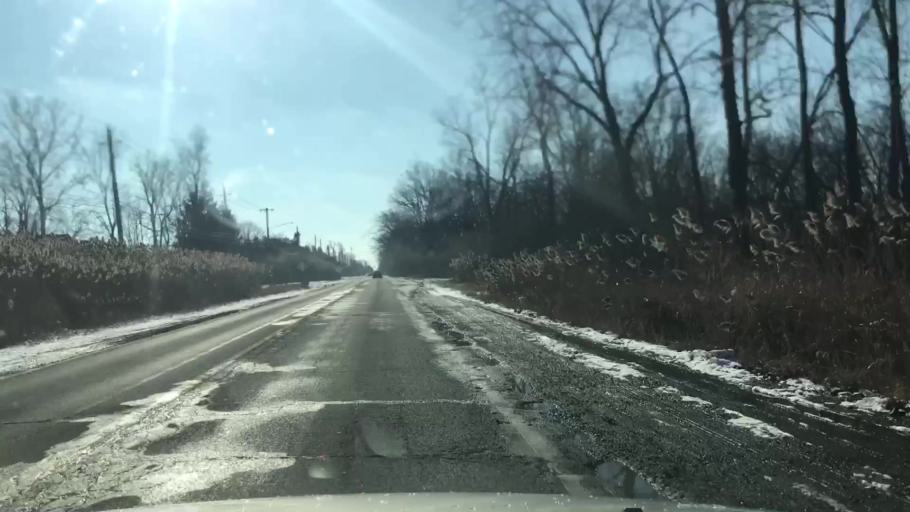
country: US
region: Michigan
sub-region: Oakland County
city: Troy
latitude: 42.6124
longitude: -83.1104
